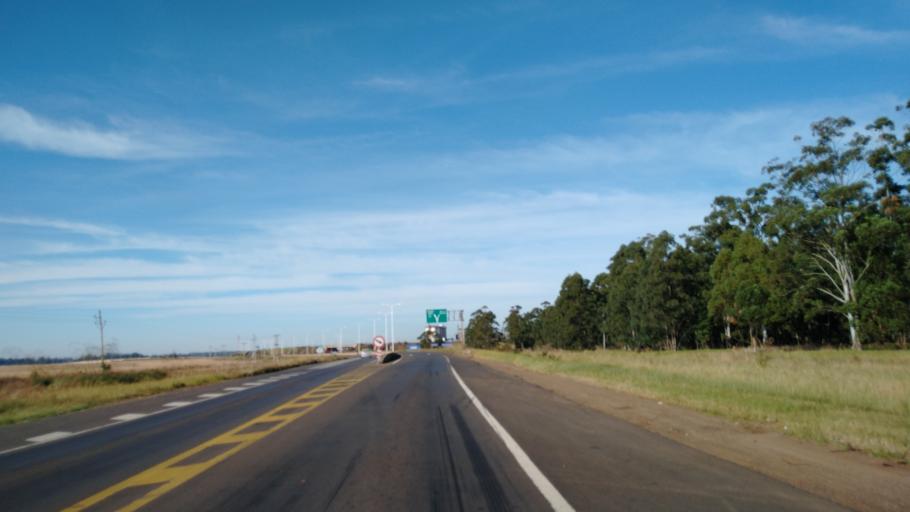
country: AR
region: Corrientes
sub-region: Departamento de Paso de los Libres
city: Paso de los Libres
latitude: -29.7053
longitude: -57.2105
